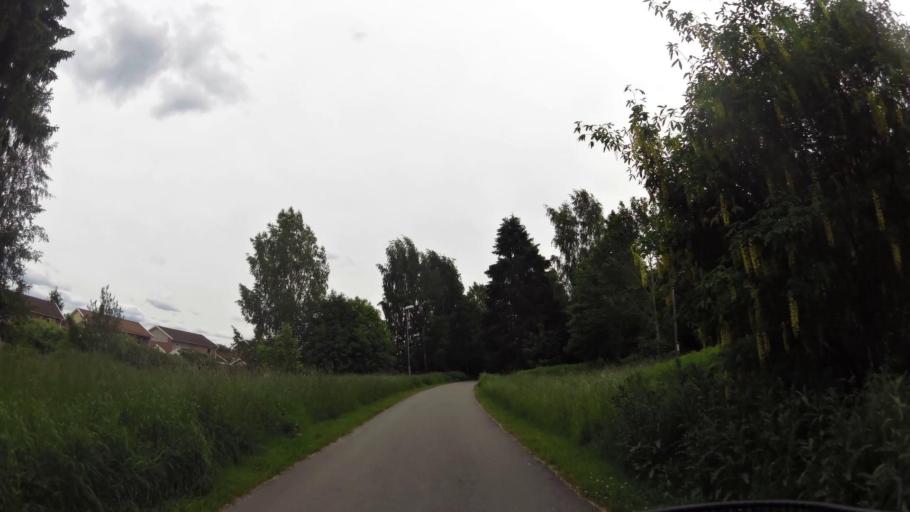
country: SE
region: OEstergoetland
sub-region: Linkopings Kommun
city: Malmslatt
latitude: 58.3790
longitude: 15.5631
